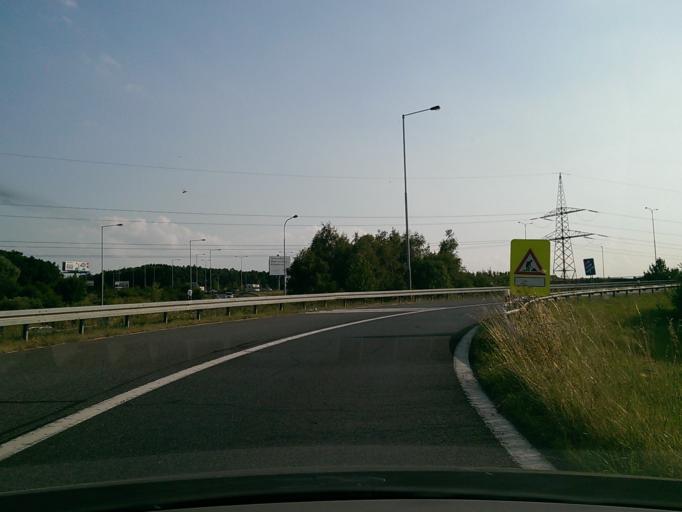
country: CZ
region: Praha
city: Cerny Most
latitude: 50.0986
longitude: 14.5946
